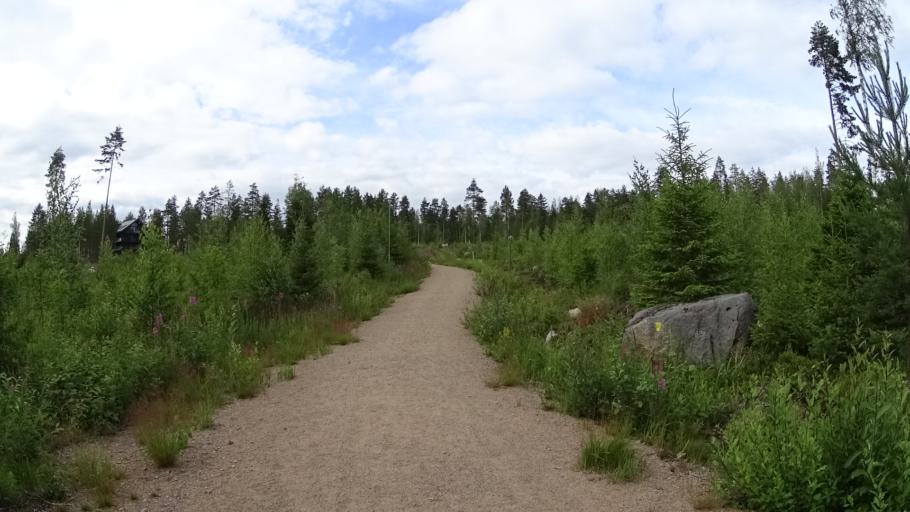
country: FI
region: Southern Ostrobothnia
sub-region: Kuusiokunnat
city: AEhtaeri
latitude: 62.5323
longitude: 24.1870
